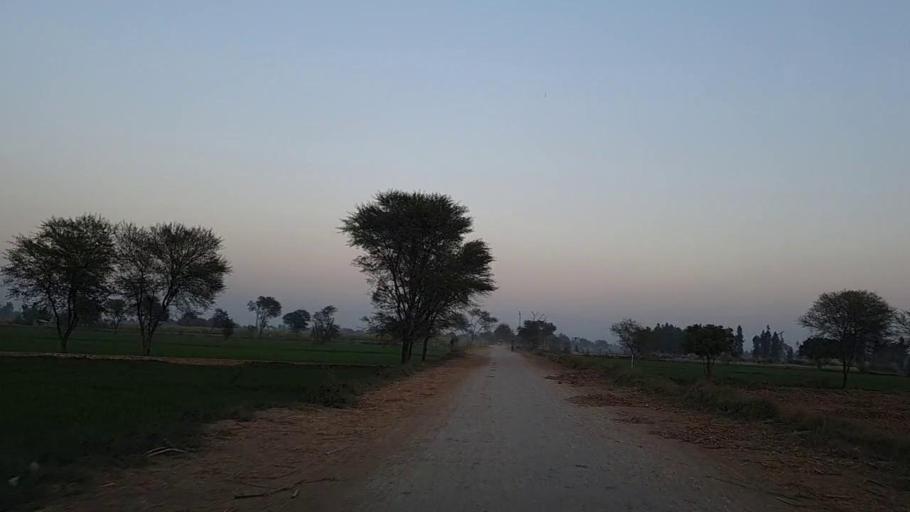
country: PK
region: Sindh
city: Naushahro Firoz
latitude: 26.8004
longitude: 68.0224
